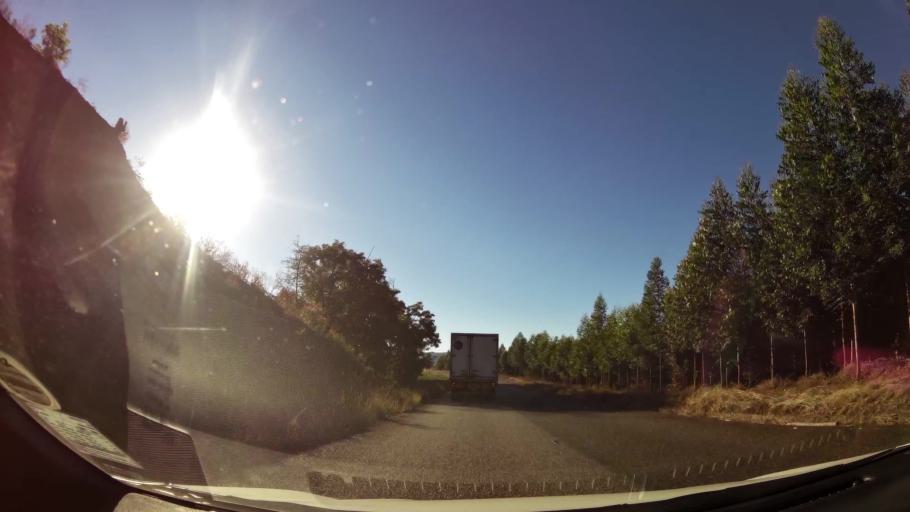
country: ZA
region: Limpopo
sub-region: Mopani District Municipality
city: Tzaneen
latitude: -23.9380
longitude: 30.0247
